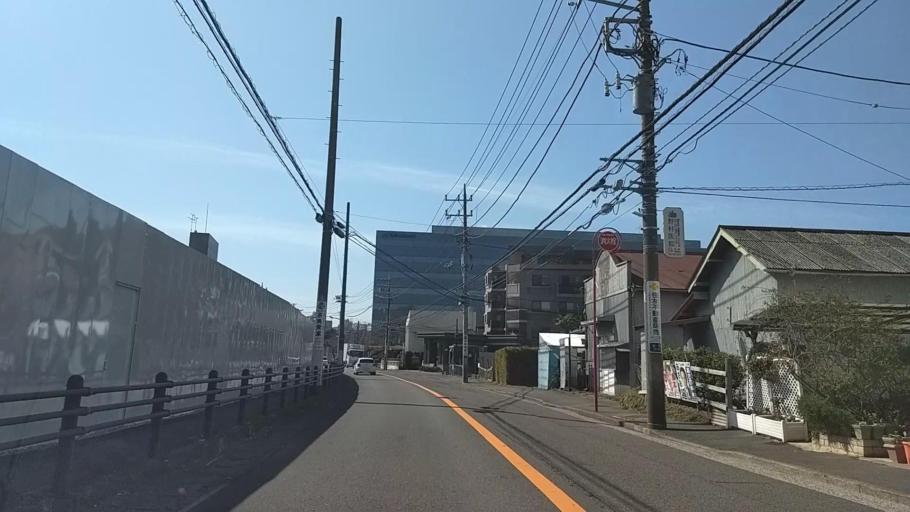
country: JP
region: Kanagawa
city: Kamakura
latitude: 35.3565
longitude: 139.5374
